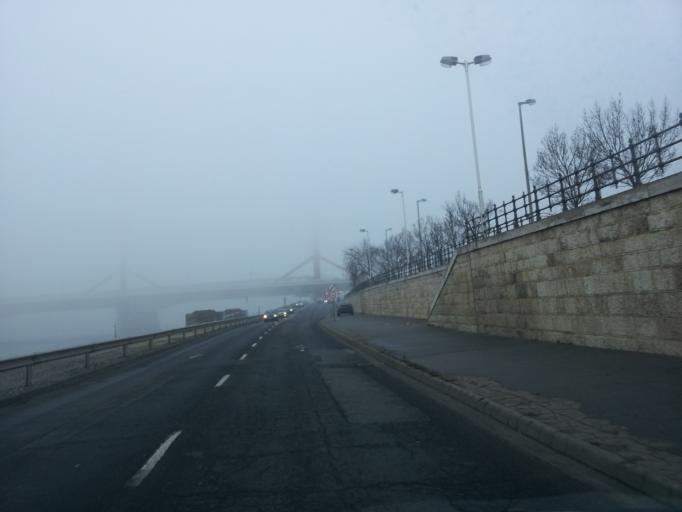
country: HU
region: Budapest
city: Budapest IX. keruelet
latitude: 47.4715
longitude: 19.0645
